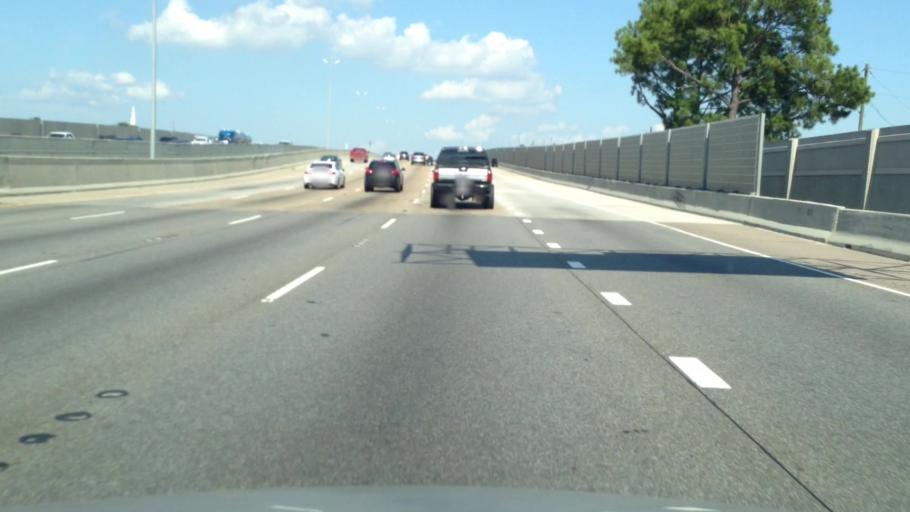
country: US
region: Louisiana
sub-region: Jefferson Parish
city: Metairie Terrace
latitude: 29.9996
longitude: -90.1959
